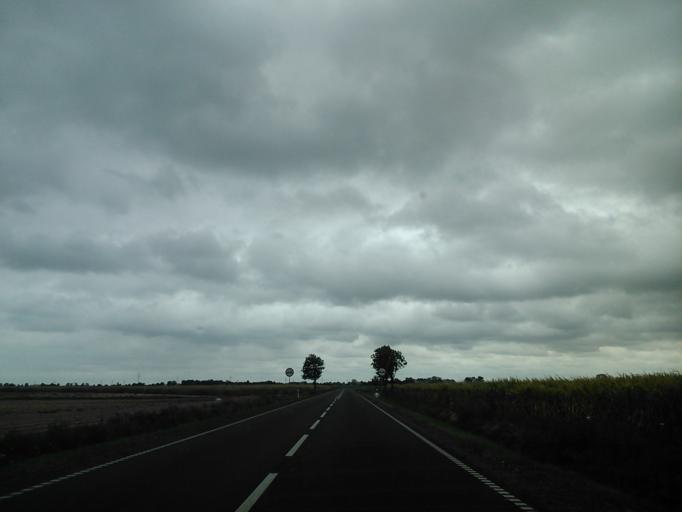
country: PL
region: Kujawsko-Pomorskie
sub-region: Powiat inowroclawski
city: Kruszwica
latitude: 52.6347
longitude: 18.3888
